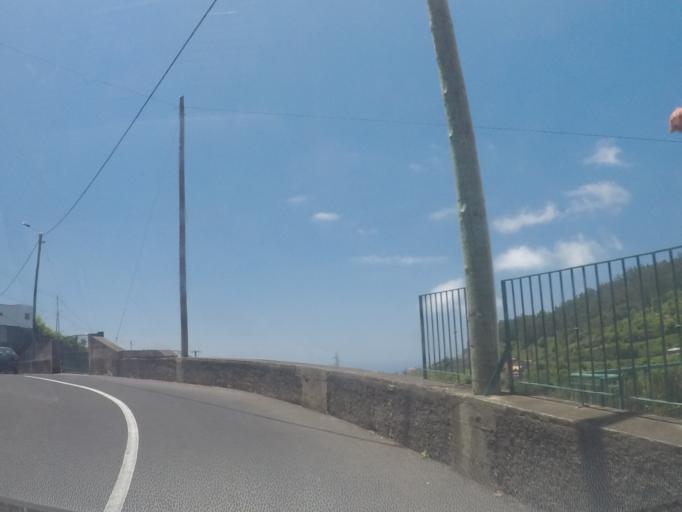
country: PT
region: Madeira
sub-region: Camara de Lobos
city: Curral das Freiras
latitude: 32.6824
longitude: -16.9911
